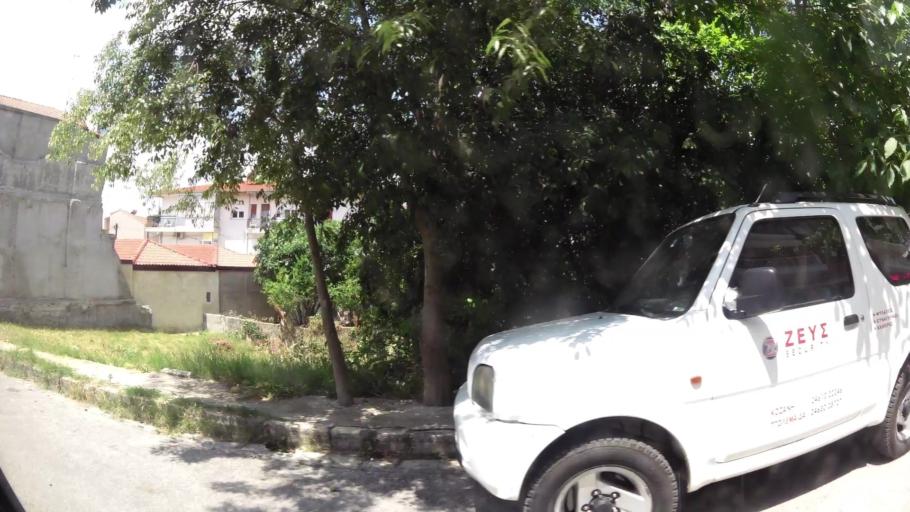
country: GR
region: West Macedonia
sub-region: Nomos Kozanis
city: Kozani
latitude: 40.2958
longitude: 21.7952
